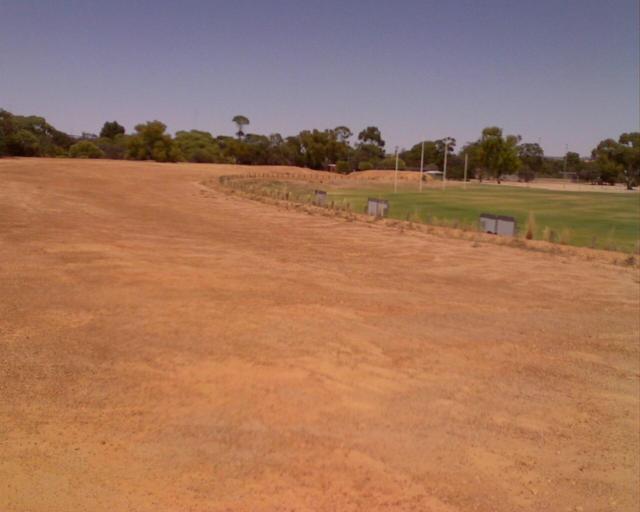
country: AU
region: Western Australia
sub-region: Wongan-Ballidu
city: Wongan Hills
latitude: -30.8205
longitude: 117.4863
